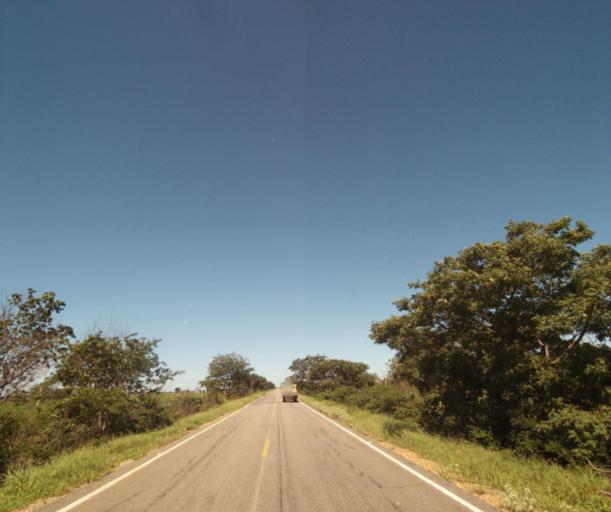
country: BR
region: Bahia
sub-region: Palmas De Monte Alto
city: Palmas de Monte Alto
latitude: -14.2645
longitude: -43.3456
